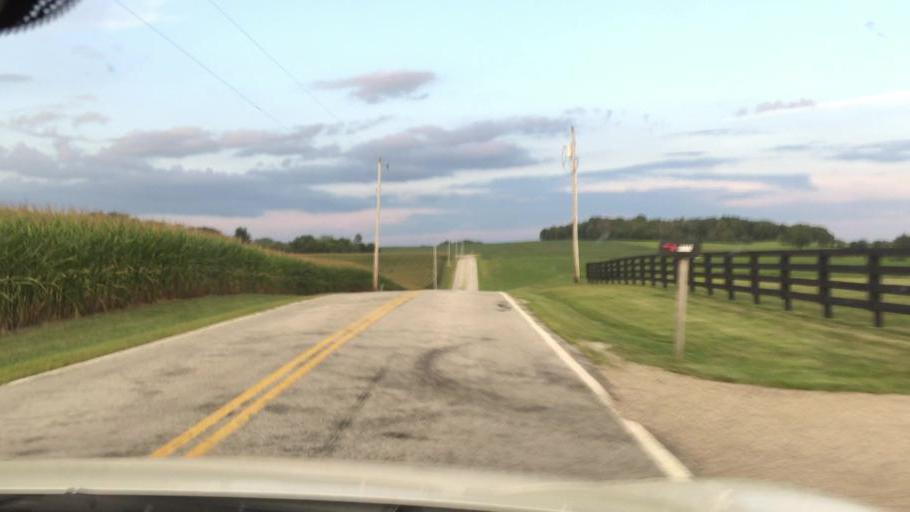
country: US
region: Ohio
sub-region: Champaign County
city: Mechanicsburg
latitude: 39.9952
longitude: -83.6449
